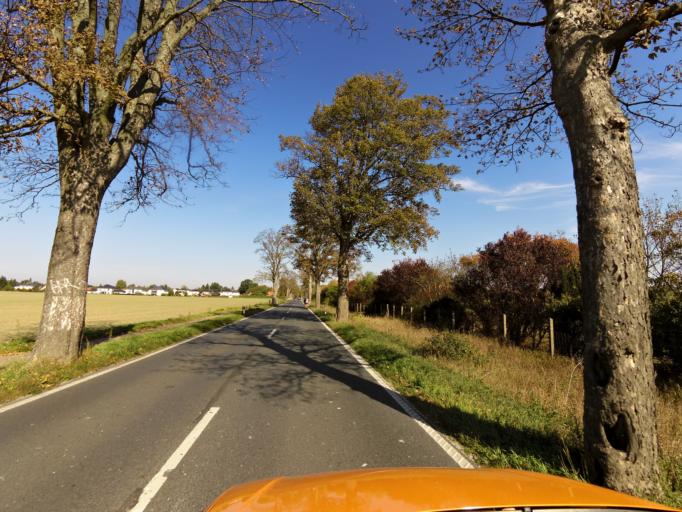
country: DE
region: Brandenburg
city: Stahnsdorf
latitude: 52.3738
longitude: 13.2030
